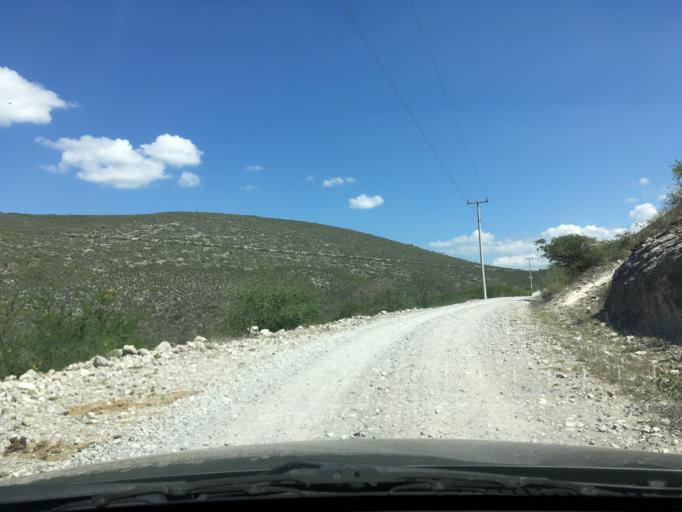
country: MX
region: Hidalgo
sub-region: Metztitlan
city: Fontezuelas
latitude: 20.6349
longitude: -98.8454
